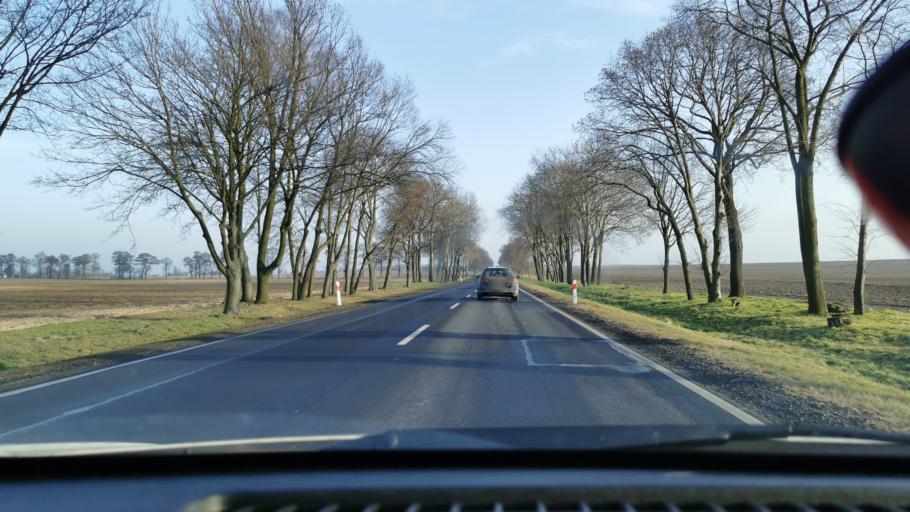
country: PL
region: Lodz Voivodeship
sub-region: Powiat sieradzki
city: Wroblew
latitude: 51.6215
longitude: 18.5817
